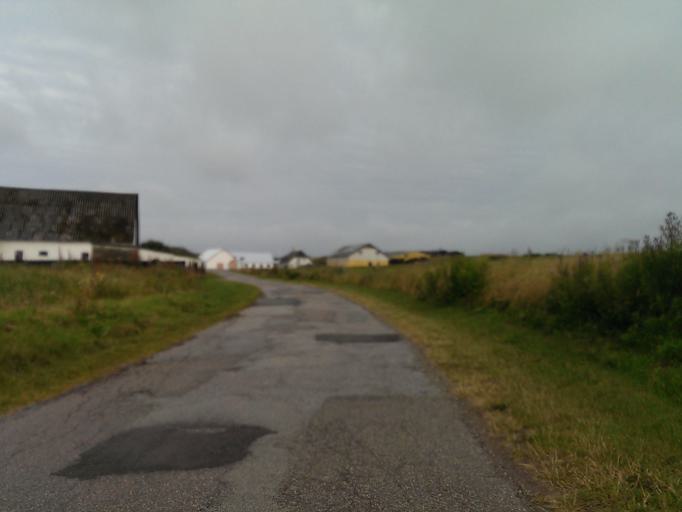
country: DK
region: North Denmark
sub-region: Jammerbugt Kommune
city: Pandrup
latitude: 57.3808
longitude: 9.7279
